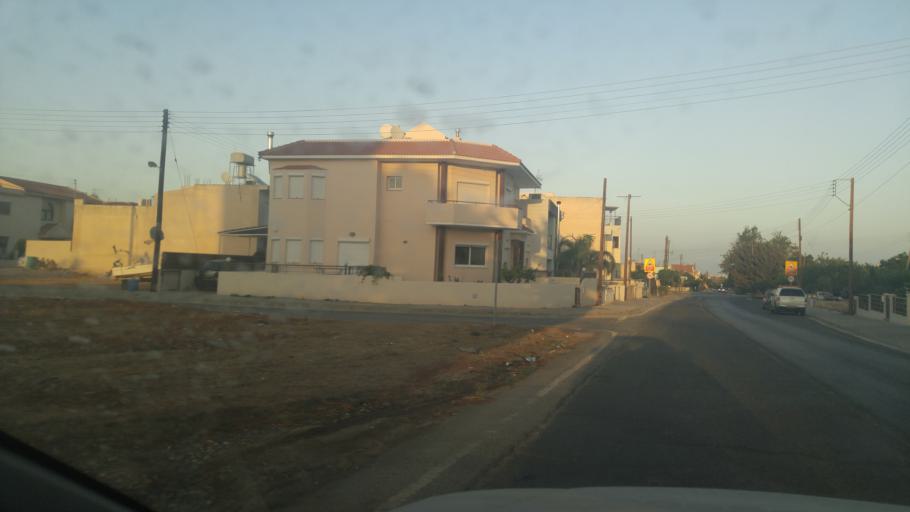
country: CY
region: Limassol
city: Ypsonas
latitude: 34.6871
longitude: 32.9716
